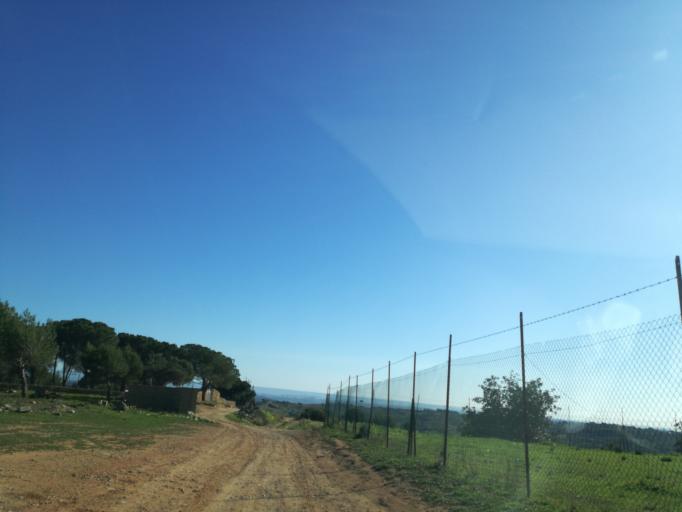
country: IT
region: Sicily
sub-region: Provincia di Caltanissetta
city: Niscemi
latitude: 37.0548
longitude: 14.3635
